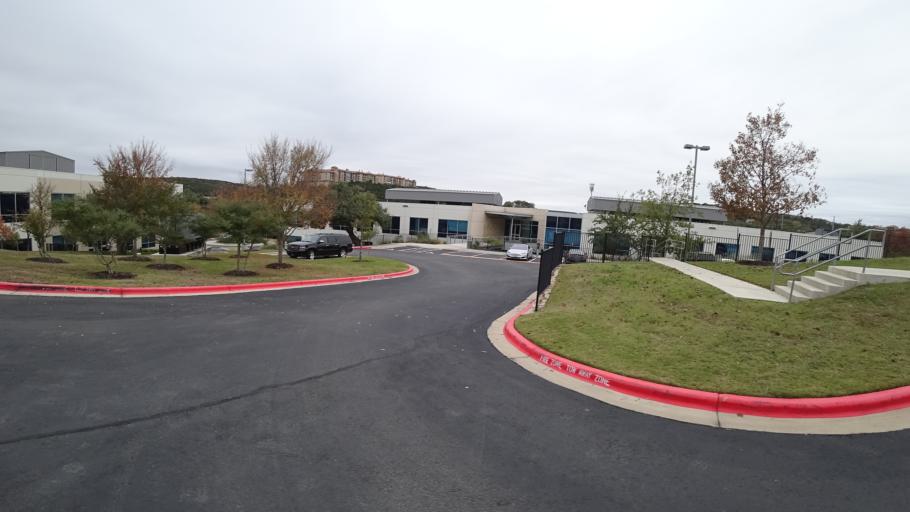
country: US
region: Texas
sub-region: Williamson County
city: Jollyville
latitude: 30.3740
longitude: -97.8022
